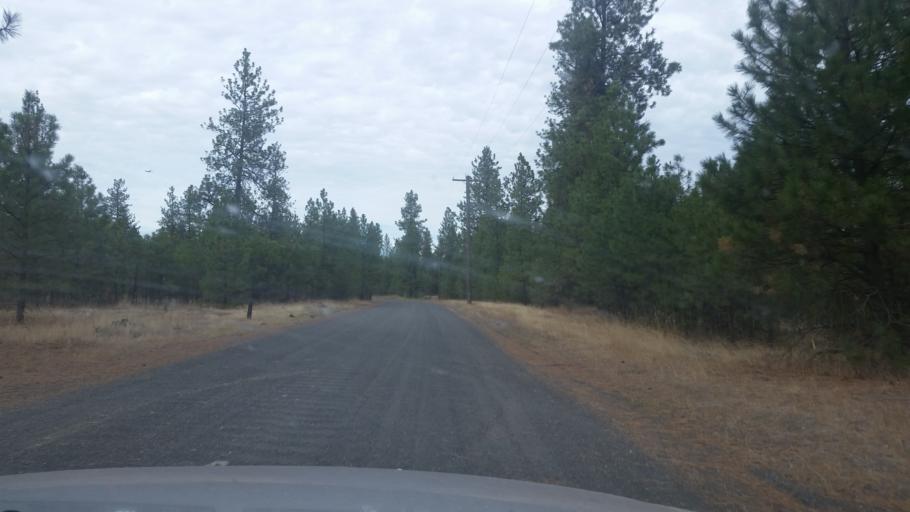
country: US
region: Washington
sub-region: Spokane County
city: Cheney
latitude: 47.5146
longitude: -117.5654
